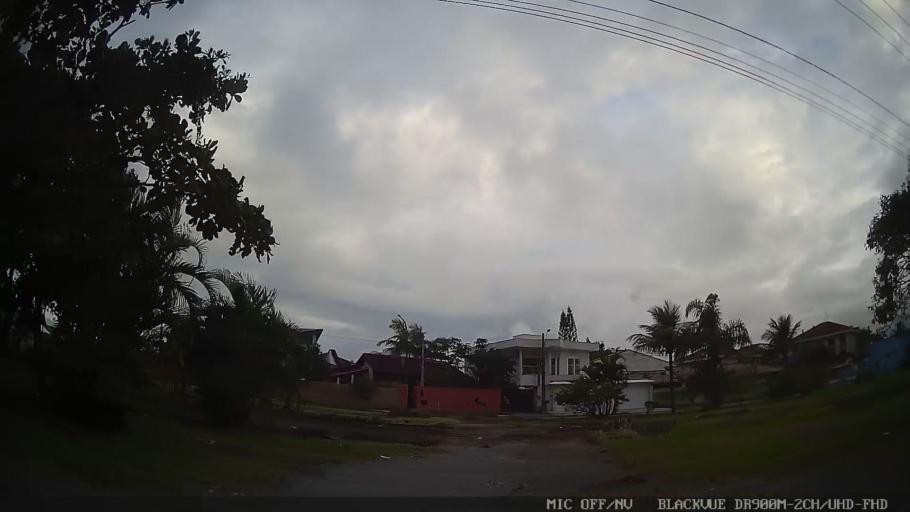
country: BR
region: Sao Paulo
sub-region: Itanhaem
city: Itanhaem
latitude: -24.1767
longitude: -46.7778
